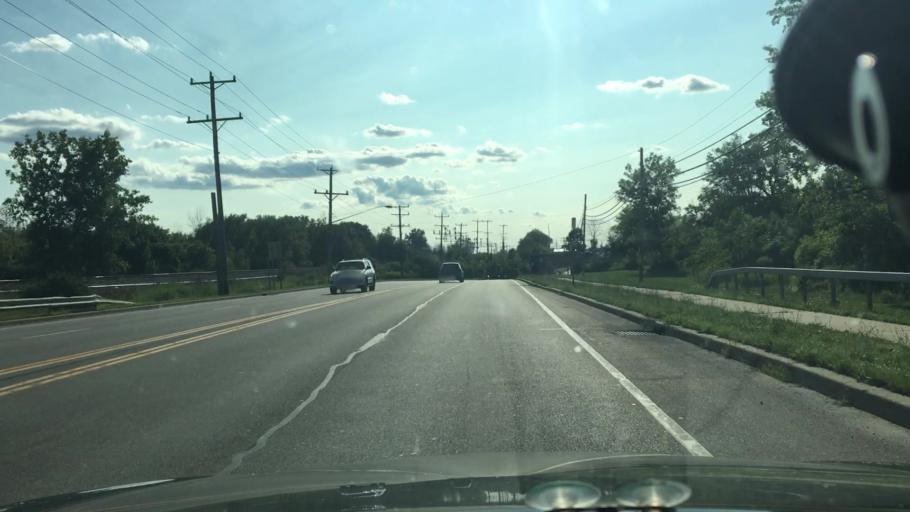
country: US
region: New York
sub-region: Erie County
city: Depew
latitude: 42.9090
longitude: -78.7156
